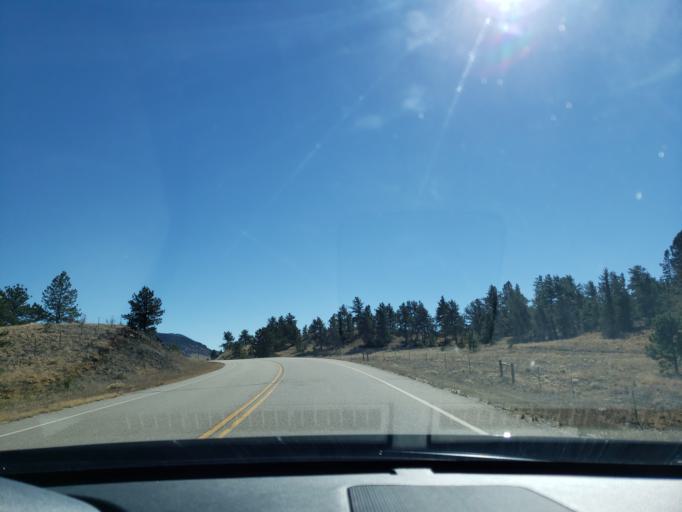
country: US
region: Colorado
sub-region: Chaffee County
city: Buena Vista
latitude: 38.8785
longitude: -105.6761
